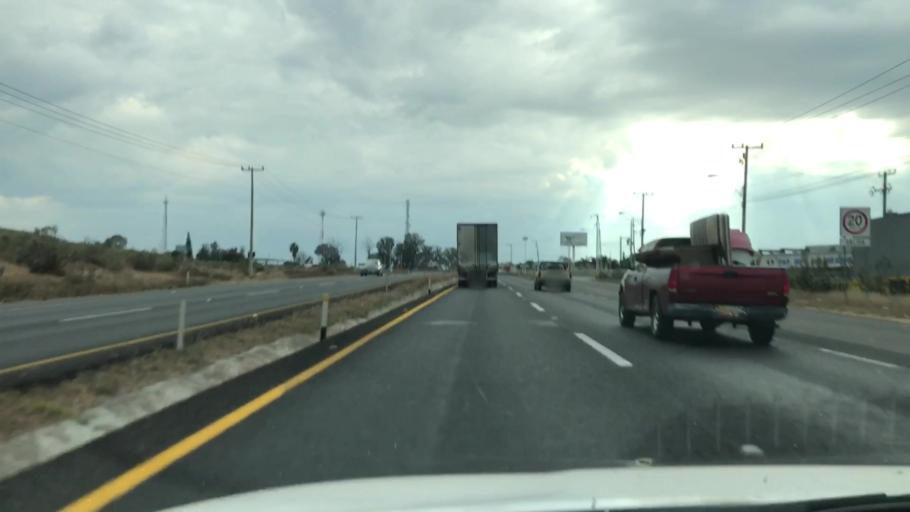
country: MX
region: Guanajuato
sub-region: Irapuato
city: San Ignacio de Rivera (Ojo de Agua)
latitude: 20.5693
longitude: -101.4448
